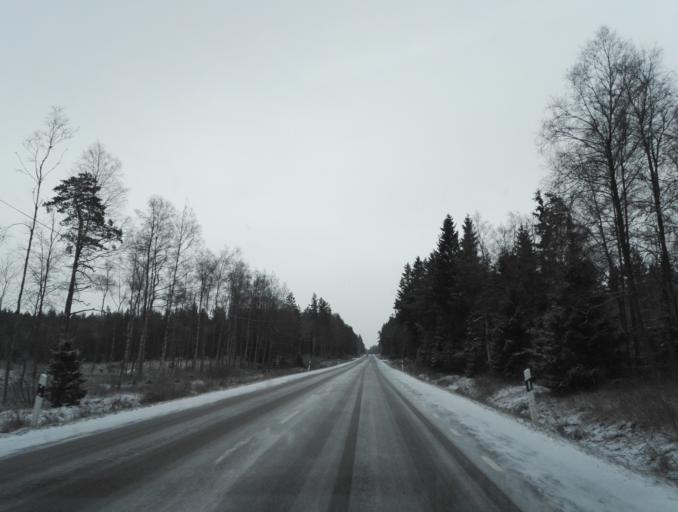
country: SE
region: Kronoberg
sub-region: Uppvidinge Kommun
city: Lenhovda
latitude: 56.9699
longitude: 15.3080
